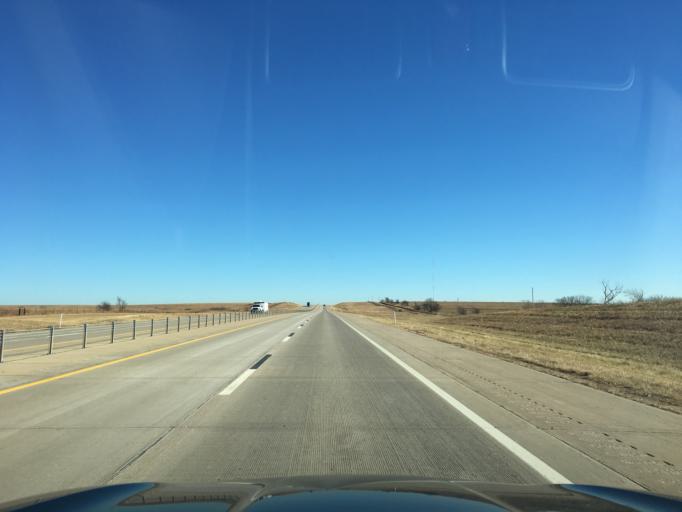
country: US
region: Oklahoma
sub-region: Noble County
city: Perry
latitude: 36.3920
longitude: -97.1605
